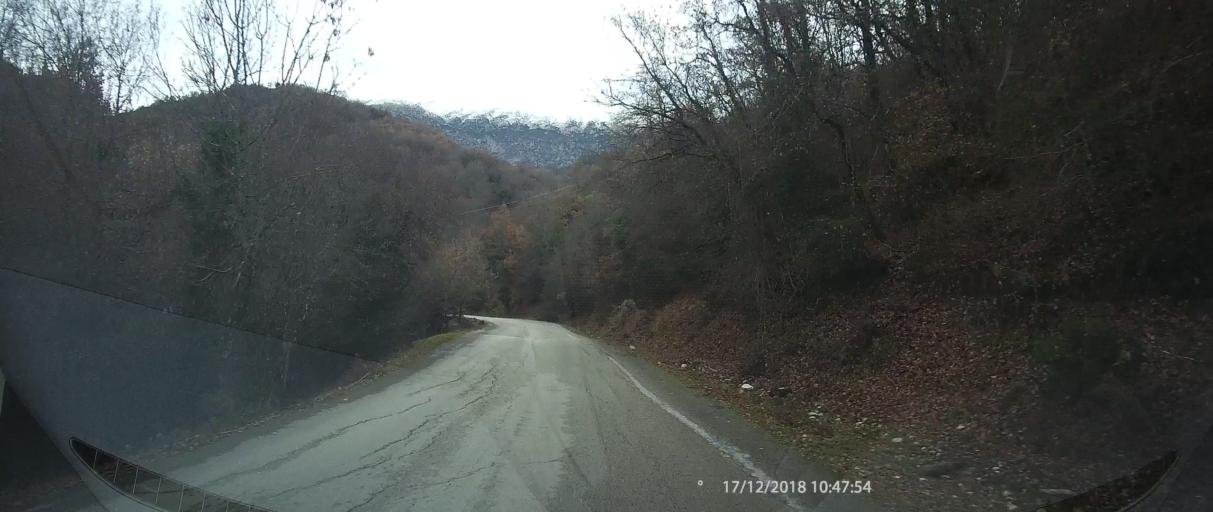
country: GR
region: Epirus
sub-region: Nomos Ioanninon
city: Konitsa
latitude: 39.9634
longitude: 20.7098
